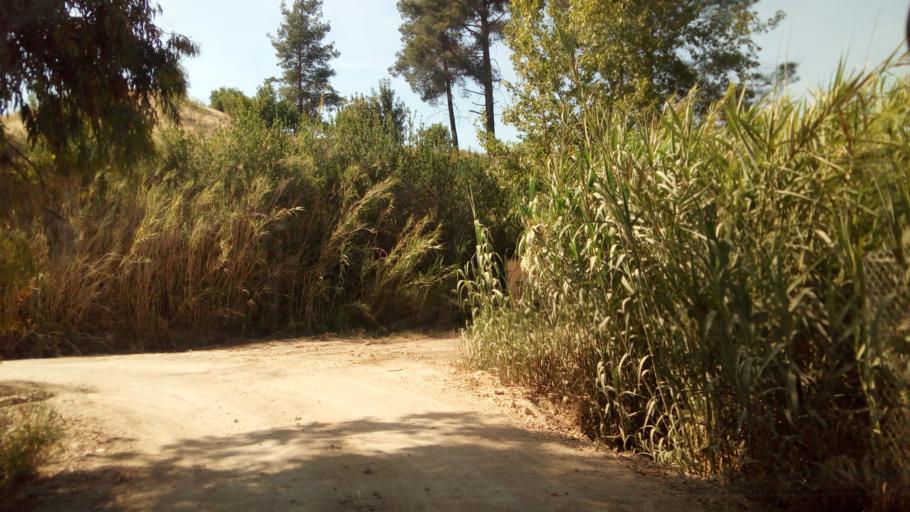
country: CY
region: Pafos
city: Polis
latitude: 34.9555
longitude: 32.5141
